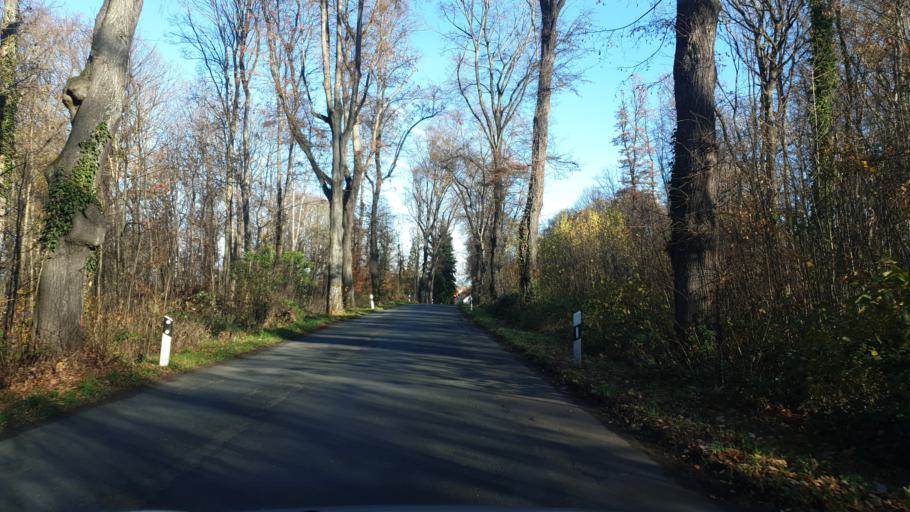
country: DE
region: Saxony-Anhalt
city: Droyssig
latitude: 51.0380
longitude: 12.0272
